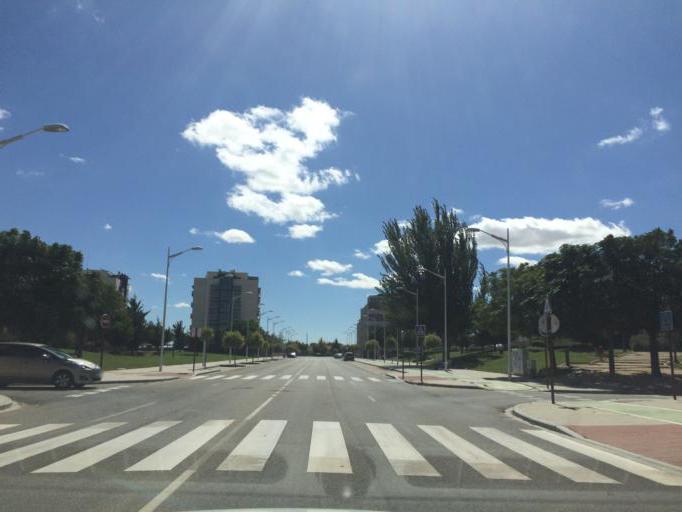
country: ES
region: Castille-La Mancha
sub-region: Provincia de Albacete
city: Albacete
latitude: 38.9798
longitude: -1.8414
